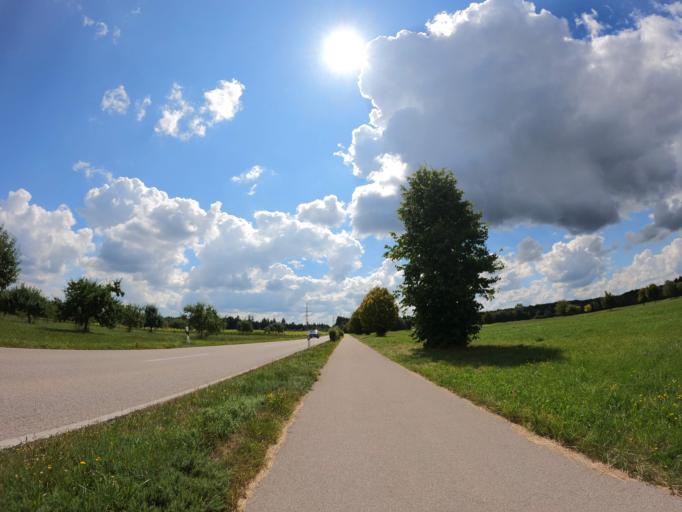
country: DE
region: Bavaria
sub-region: Upper Bavaria
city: Brunnthal
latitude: 48.0258
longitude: 11.6797
